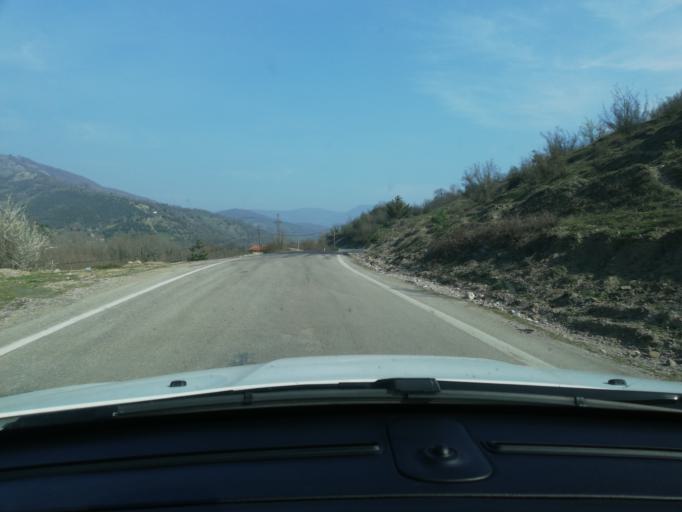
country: TR
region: Karabuk
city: Yenice
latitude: 41.2256
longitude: 32.3623
